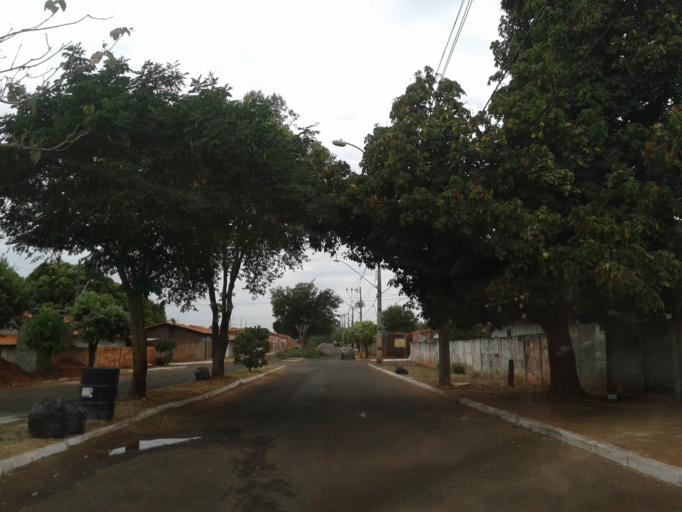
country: BR
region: Minas Gerais
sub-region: Santa Vitoria
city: Santa Vitoria
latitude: -18.8500
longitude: -50.1194
